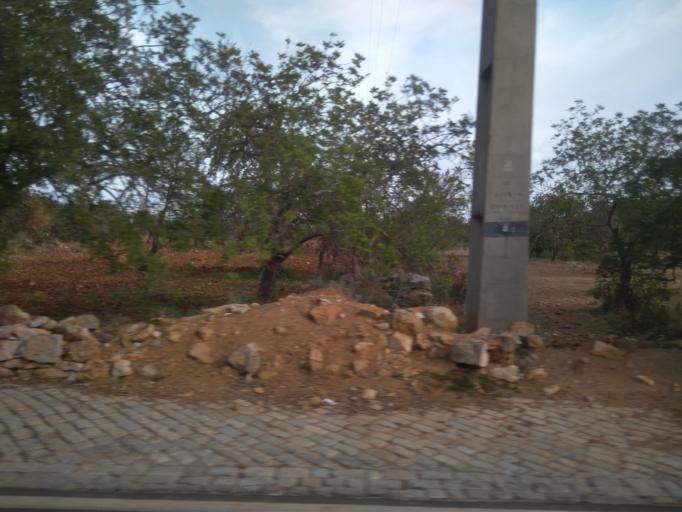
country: PT
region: Faro
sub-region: Faro
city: Santa Barbara de Nexe
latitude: 37.0979
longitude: -7.9638
